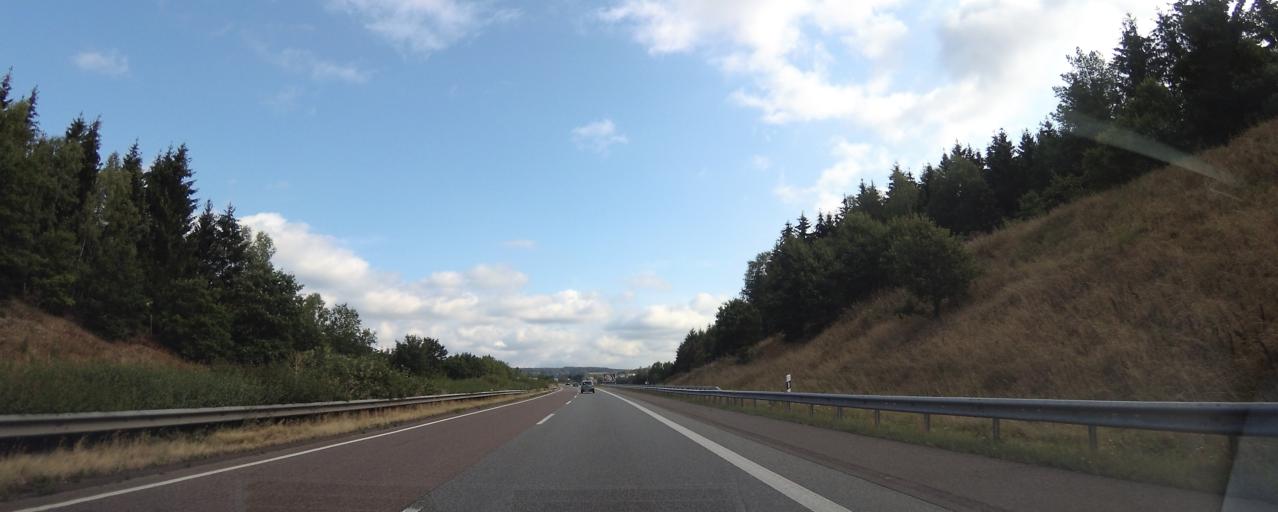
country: DE
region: Rheinland-Pfalz
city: Hermeskeil
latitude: 49.6432
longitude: 6.9256
